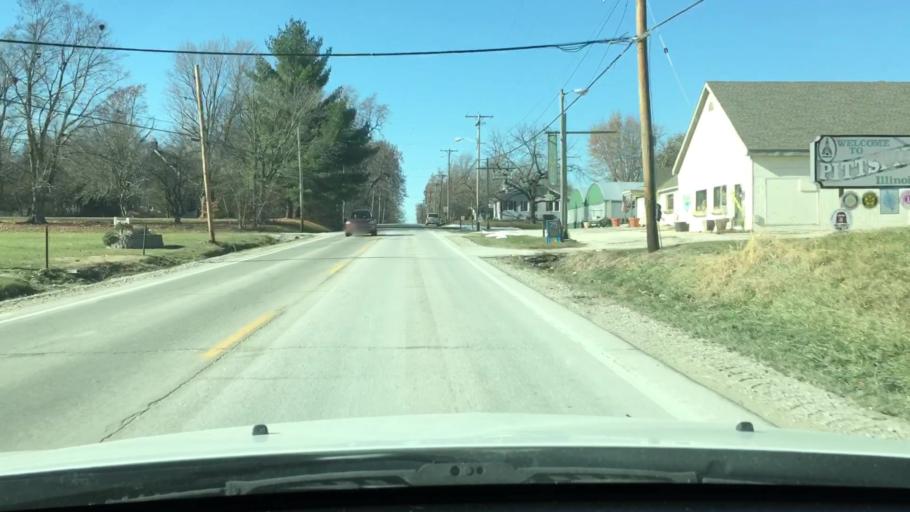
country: US
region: Illinois
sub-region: Pike County
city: Pittsfield
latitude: 39.6068
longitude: -90.7900
